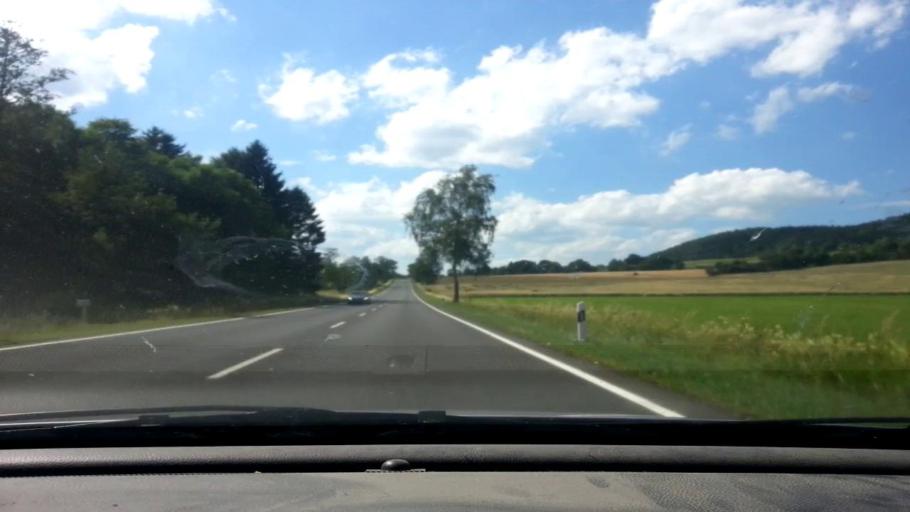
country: DE
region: Bavaria
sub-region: Upper Palatinate
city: Kastl
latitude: 49.8574
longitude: 11.9665
